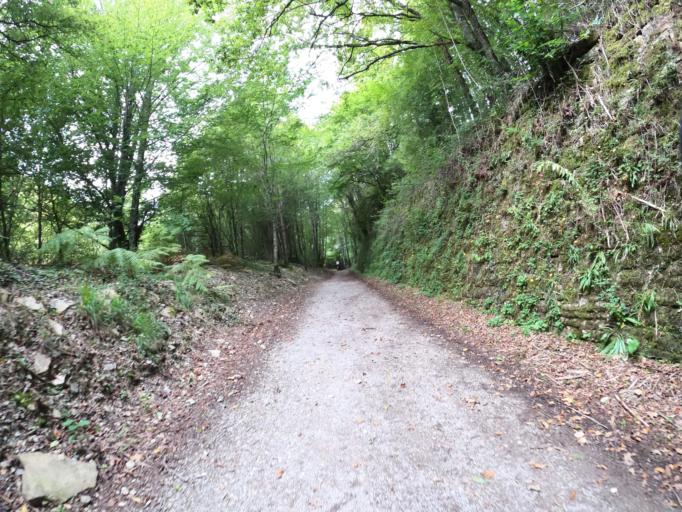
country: ES
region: Navarre
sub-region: Provincia de Navarra
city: Lekunberri
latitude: 42.9800
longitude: -1.8588
